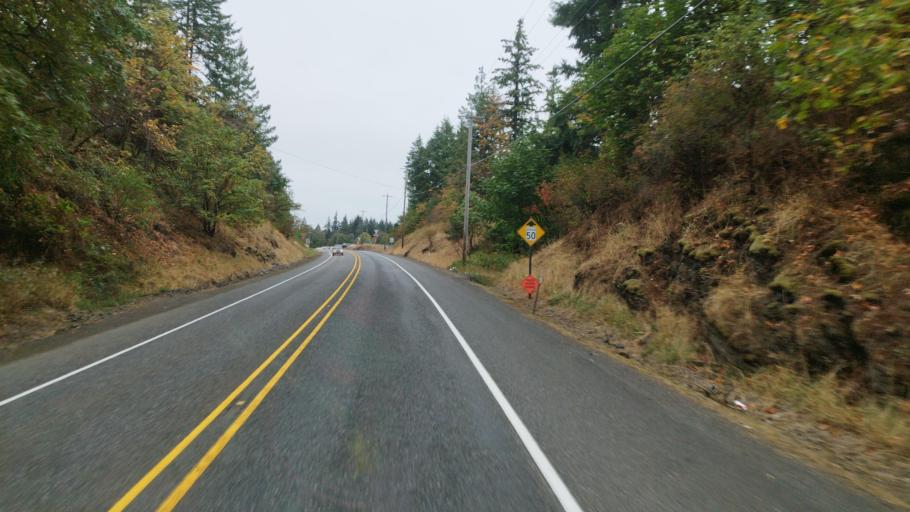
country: US
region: Oregon
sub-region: Columbia County
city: Rainier
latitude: 46.0616
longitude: -122.8953
